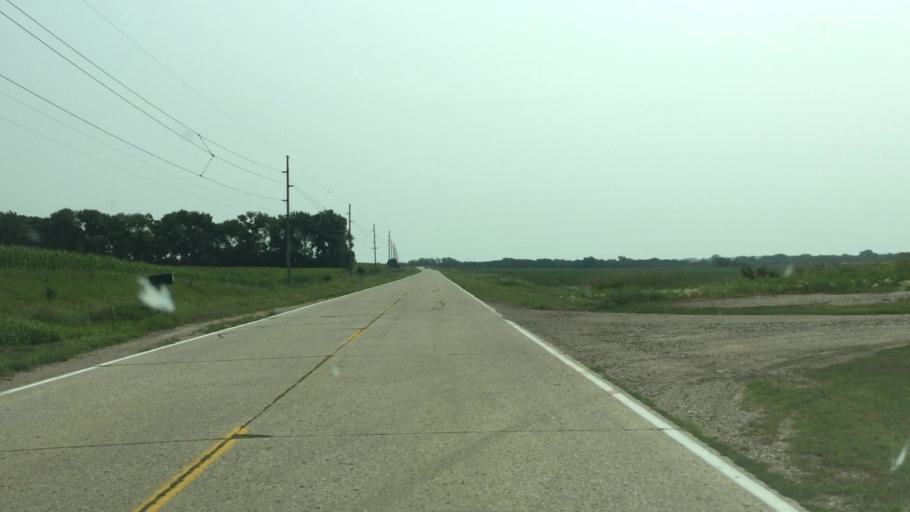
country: US
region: Iowa
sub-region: Dickinson County
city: Milford
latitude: 43.3714
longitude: -95.1950
